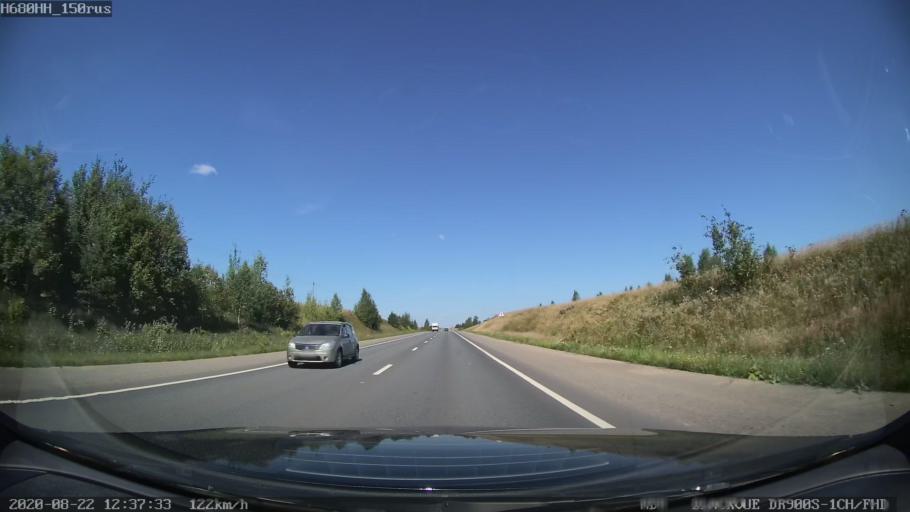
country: RU
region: Tverskaya
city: Rameshki
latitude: 57.2978
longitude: 36.0890
